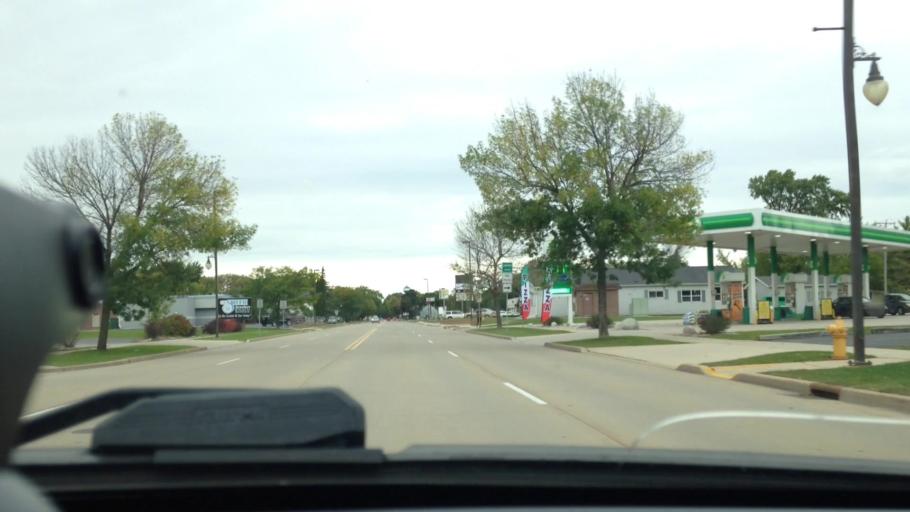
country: US
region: Wisconsin
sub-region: Fond du Lac County
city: North Fond du Lac
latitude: 43.8018
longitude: -88.4789
